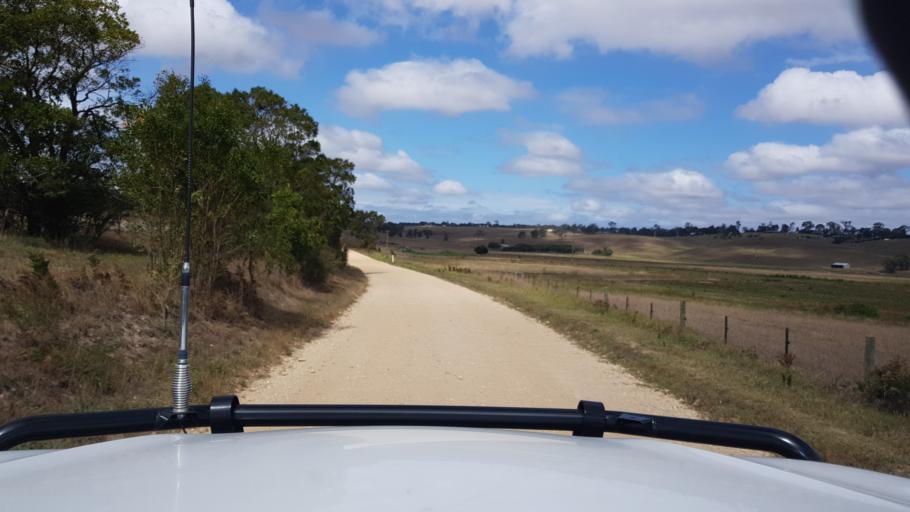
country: AU
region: Victoria
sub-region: East Gippsland
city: Bairnsdale
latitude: -37.7842
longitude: 147.5507
